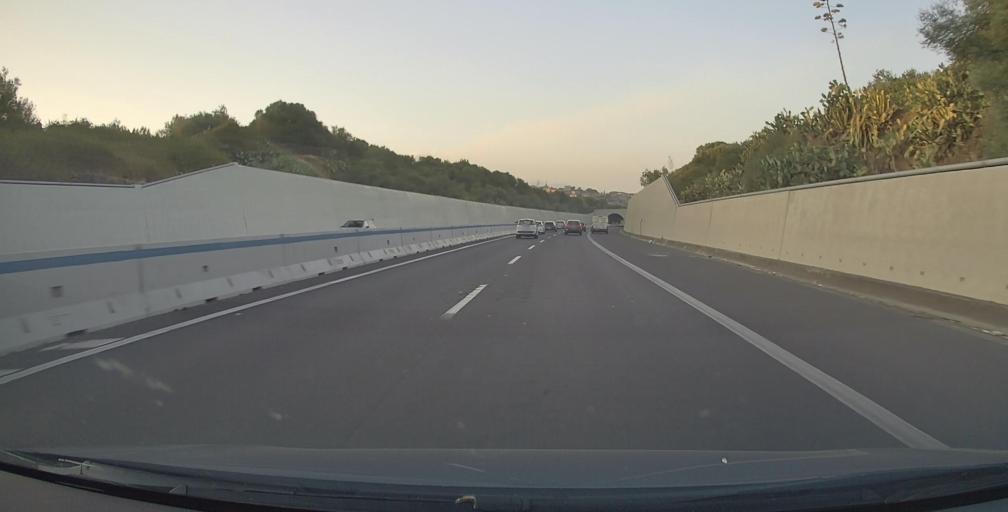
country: IT
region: Sicily
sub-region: Catania
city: Misterbianco
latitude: 37.5176
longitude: 15.0203
